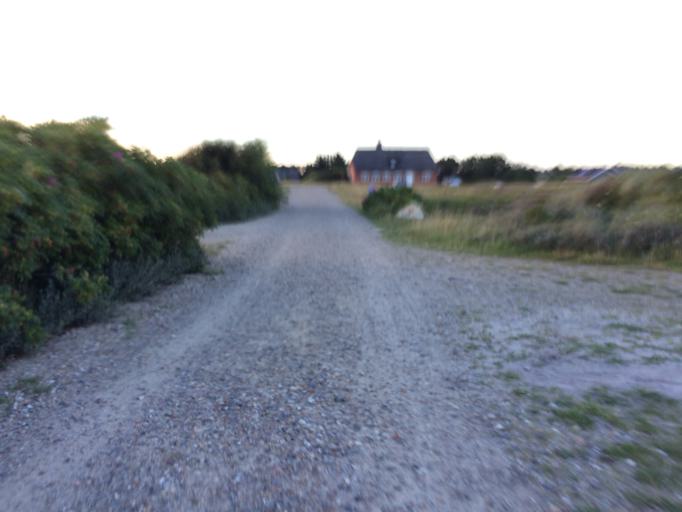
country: DK
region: Central Jutland
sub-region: Ringkobing-Skjern Kommune
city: Hvide Sande
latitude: 55.8799
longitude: 8.1684
